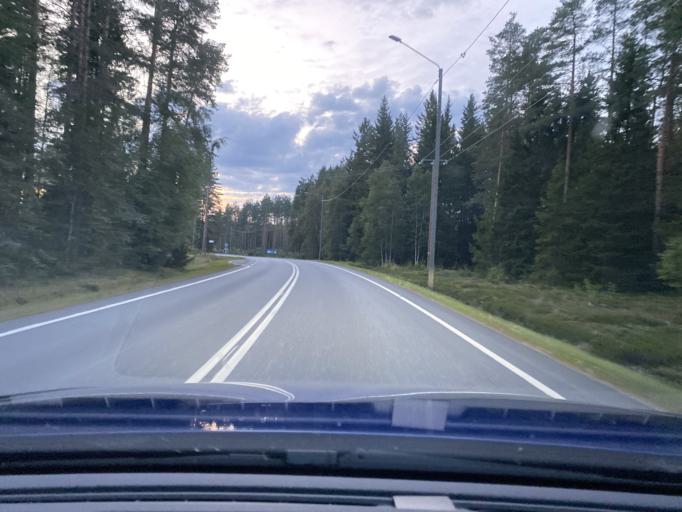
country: FI
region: Satakunta
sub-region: Pohjois-Satakunta
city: Honkajoki
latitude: 62.2118
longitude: 22.2996
